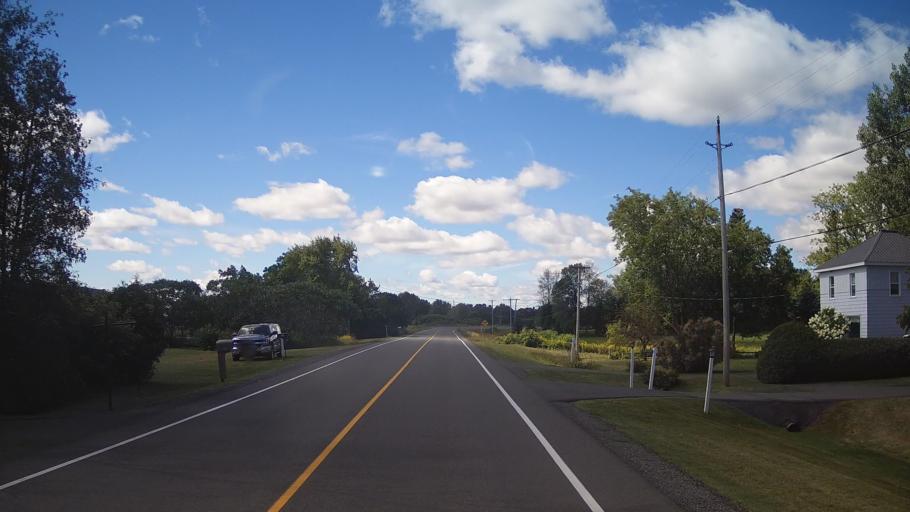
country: US
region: New York
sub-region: St. Lawrence County
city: Ogdensburg
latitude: 44.8593
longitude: -75.2680
